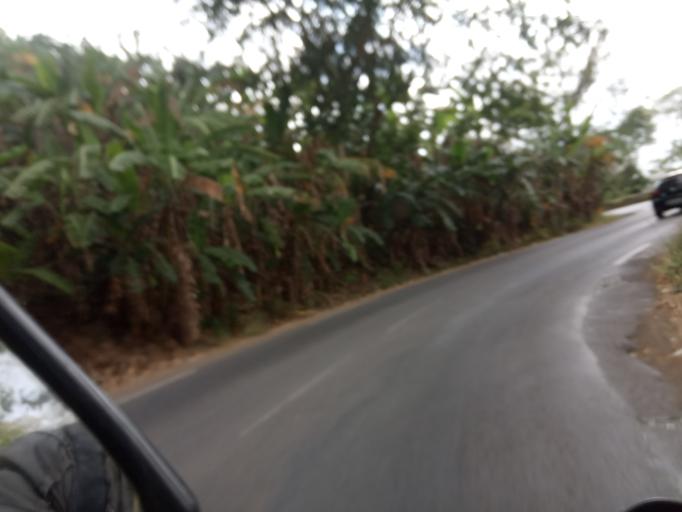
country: YT
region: Dembeni
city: Dembeni
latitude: -12.8367
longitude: 45.1816
